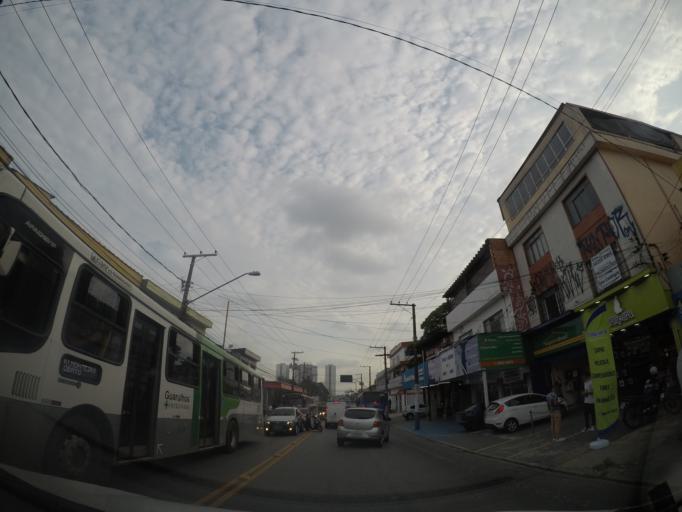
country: BR
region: Sao Paulo
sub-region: Guarulhos
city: Guarulhos
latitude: -23.4495
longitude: -46.5085
